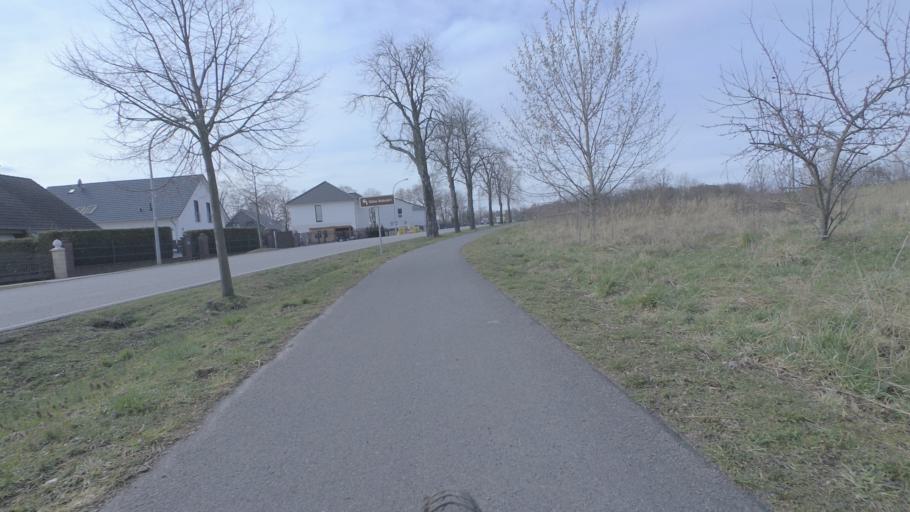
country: DE
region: Brandenburg
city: Grossbeeren
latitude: 52.3422
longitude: 13.3590
